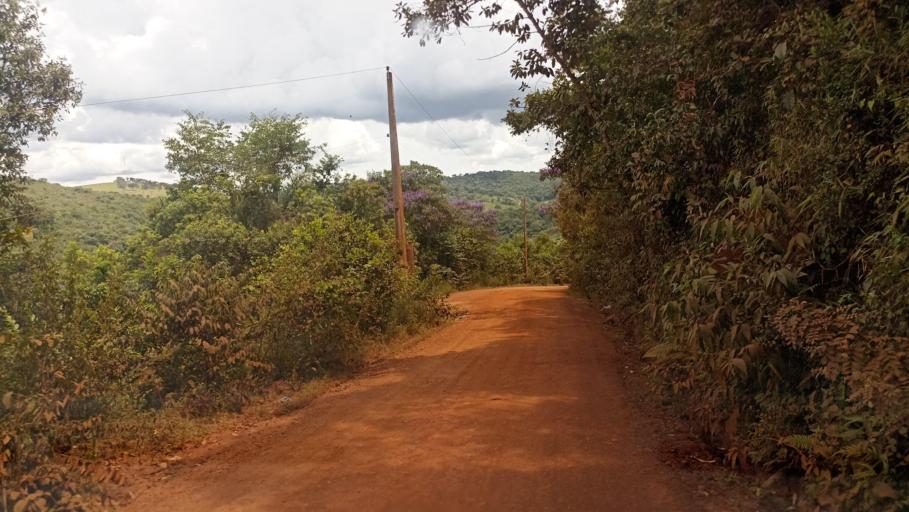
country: BR
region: Minas Gerais
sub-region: Itabirito
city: Itabirito
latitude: -20.3377
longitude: -43.7618
